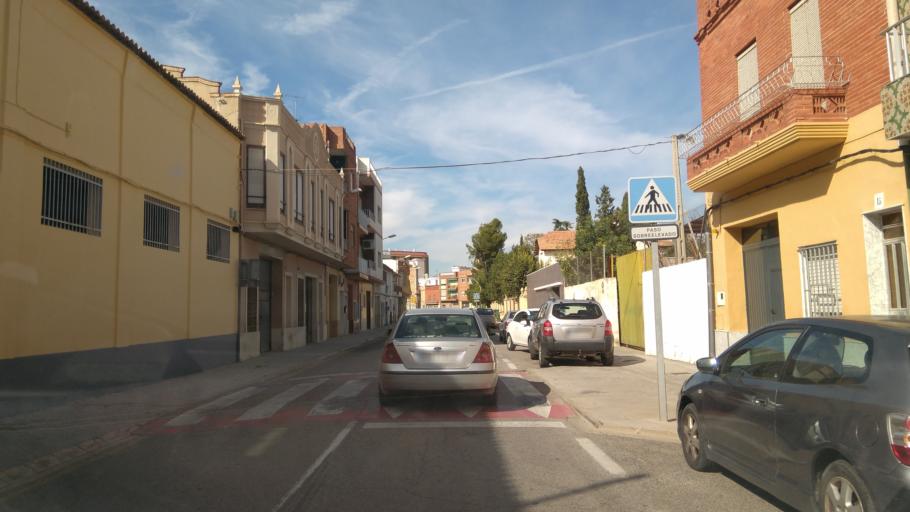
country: ES
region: Valencia
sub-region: Provincia de Valencia
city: Real de Montroi
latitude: 39.3351
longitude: -0.6076
